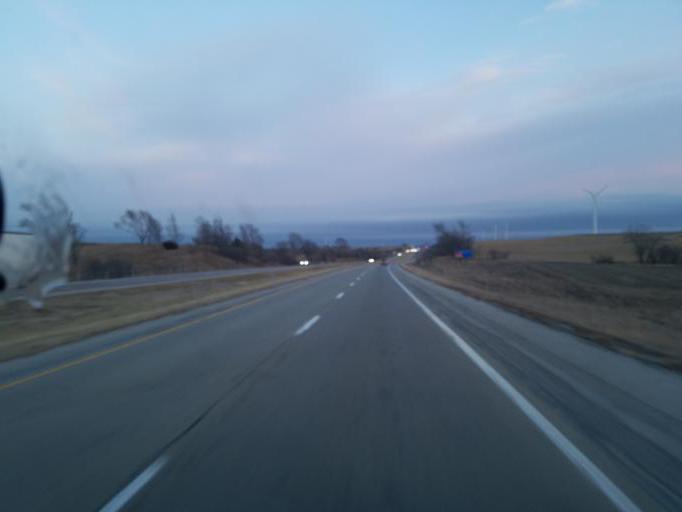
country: US
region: Iowa
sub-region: Pottawattamie County
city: Avoca
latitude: 41.4986
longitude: -95.2879
